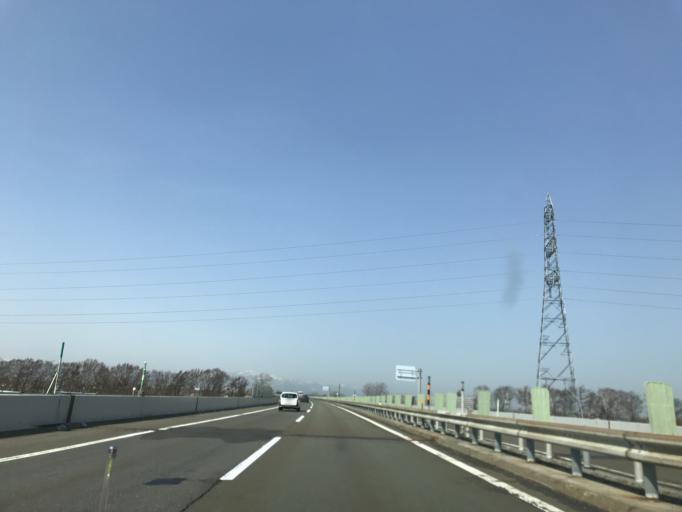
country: JP
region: Hokkaido
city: Ebetsu
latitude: 43.0946
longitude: 141.4868
